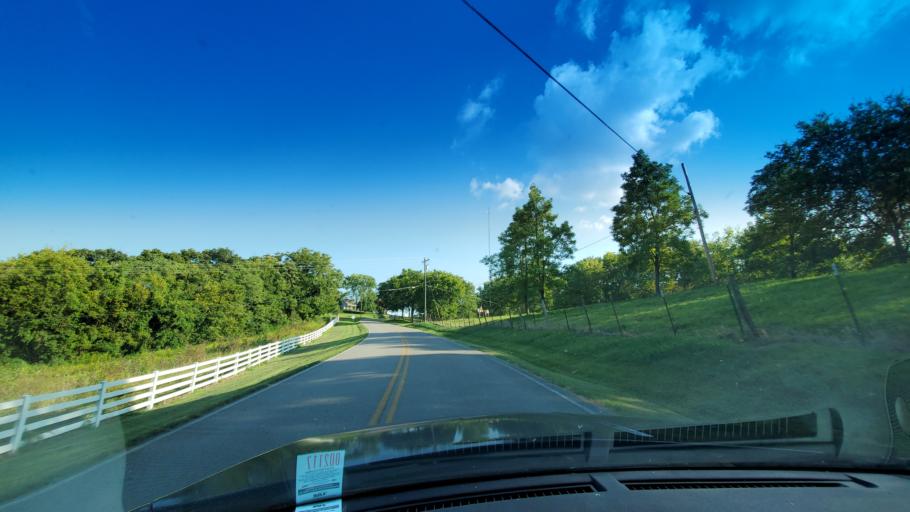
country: US
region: Tennessee
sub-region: Wilson County
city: Lebanon
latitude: 36.1606
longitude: -86.3745
